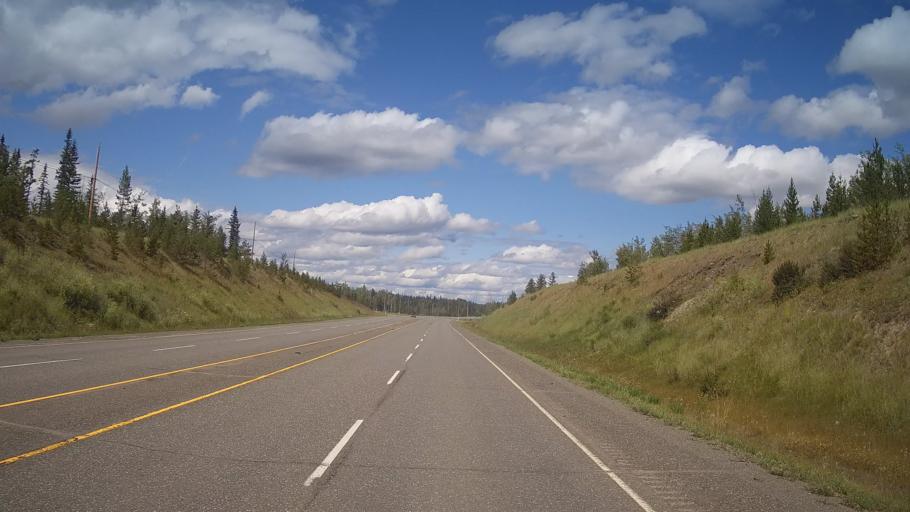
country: CA
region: British Columbia
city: Cache Creek
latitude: 51.4933
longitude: -121.3691
